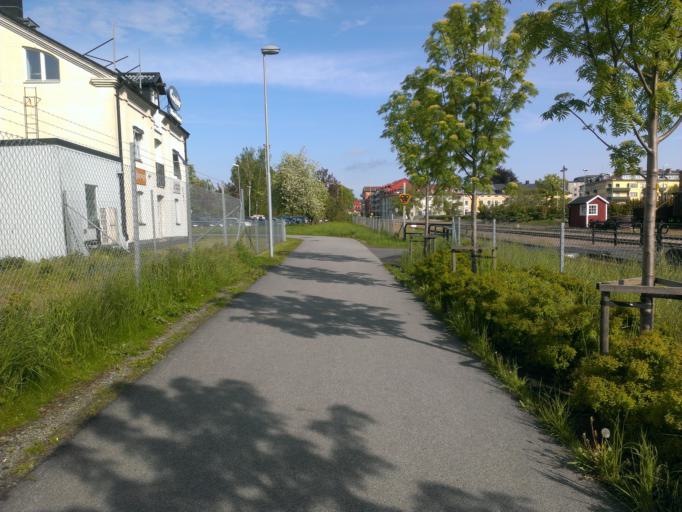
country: SE
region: Skane
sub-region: Kristianstads Kommun
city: Kristianstad
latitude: 56.0231
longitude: 14.1608
